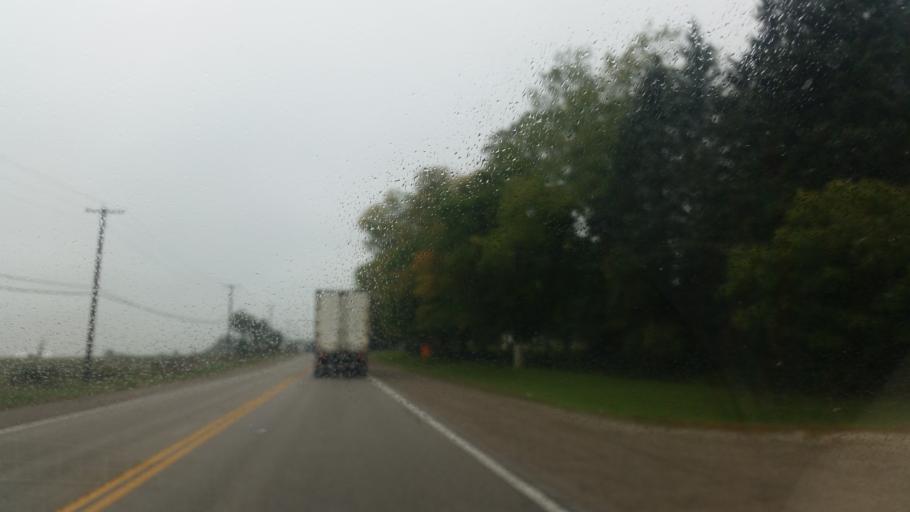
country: CA
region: Ontario
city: Waterloo
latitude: 43.6857
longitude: -80.4414
